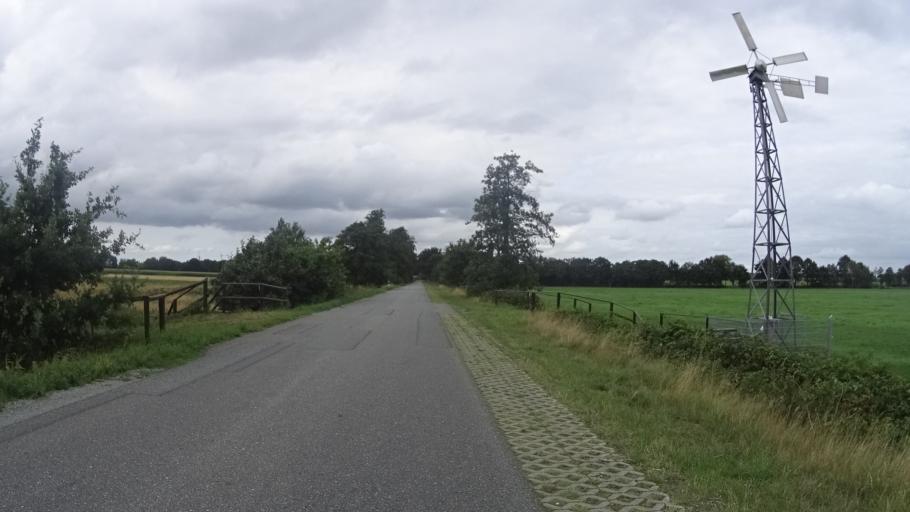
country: DE
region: Lower Saxony
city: Stinstedt
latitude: 53.6491
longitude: 8.9618
